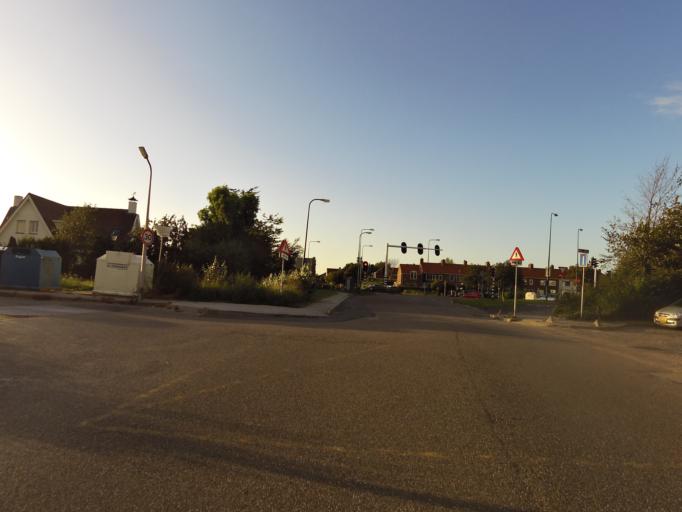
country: NL
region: South Holland
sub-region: Gemeente Katwijk
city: Rijnsburg
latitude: 52.1782
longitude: 4.4518
